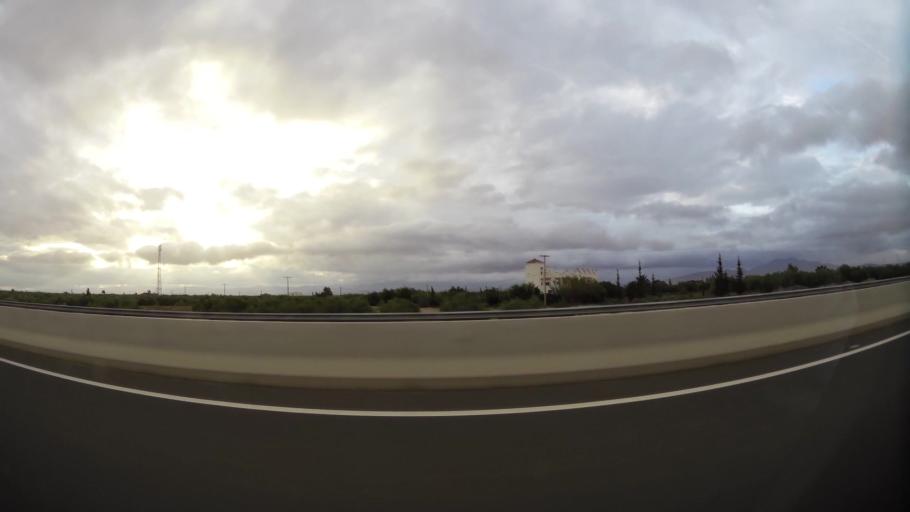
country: MA
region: Taza-Al Hoceima-Taounate
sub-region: Taza
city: Guercif
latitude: 34.3538
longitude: -3.3075
